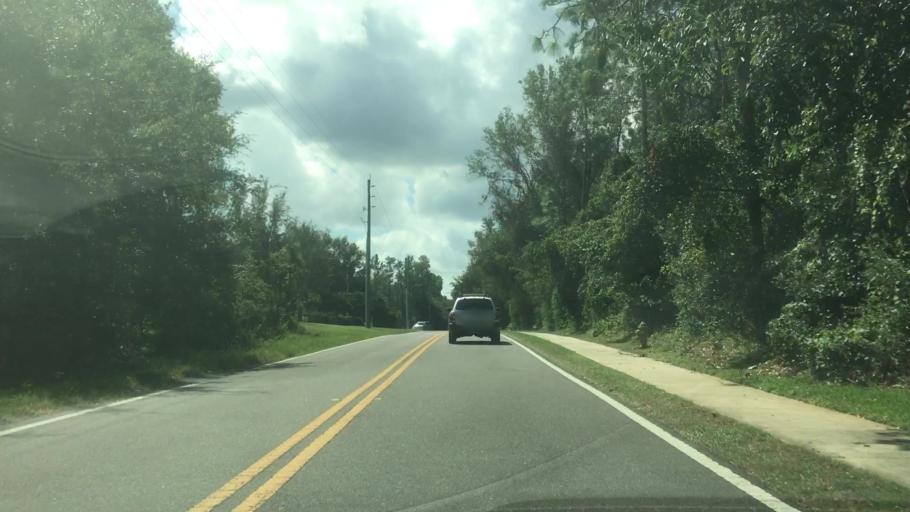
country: US
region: Florida
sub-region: Duval County
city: Jacksonville
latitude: 30.4499
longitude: -81.5791
